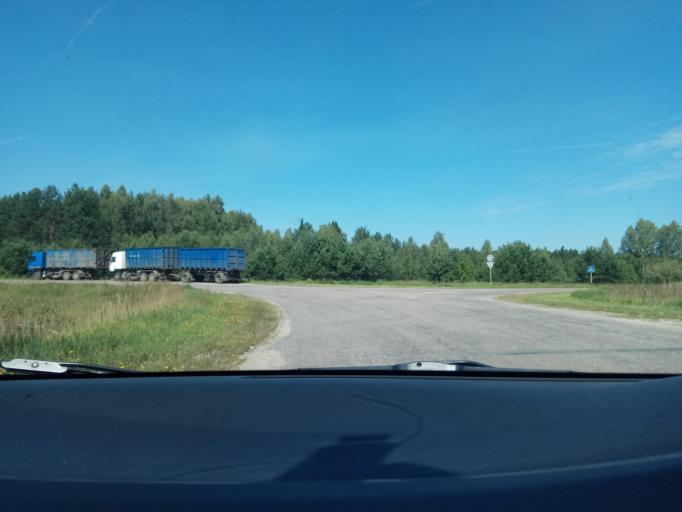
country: RU
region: Vladimir
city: Dobryatino
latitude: 55.7322
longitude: 41.4308
